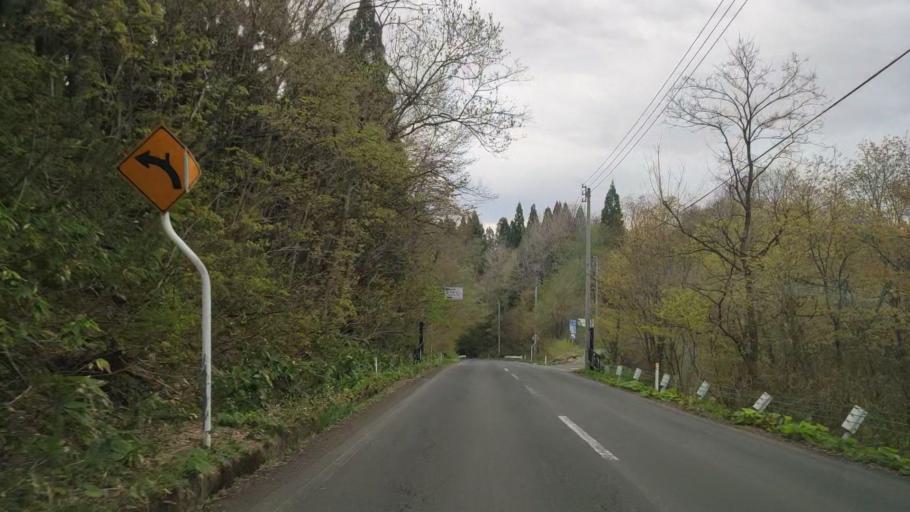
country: JP
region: Akita
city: Hanawa
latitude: 40.3707
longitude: 140.7839
